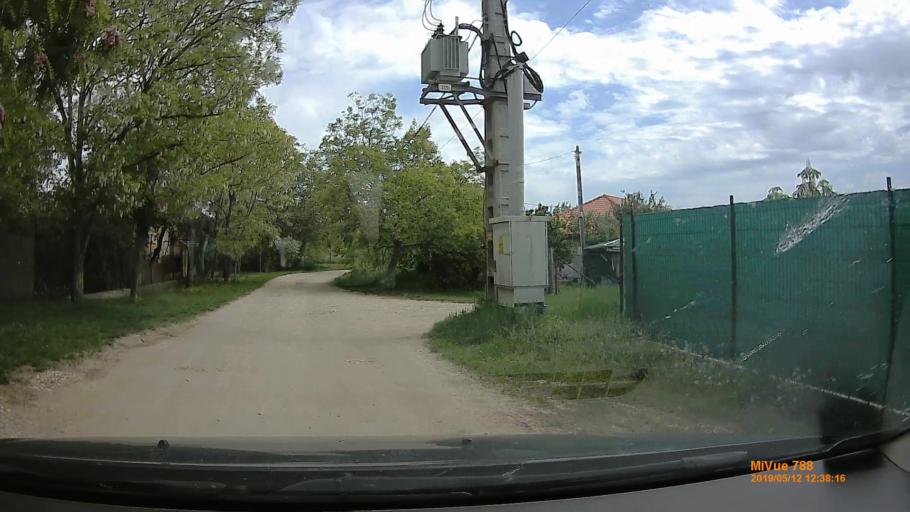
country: HU
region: Pest
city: Ecser
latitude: 47.4567
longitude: 19.3092
